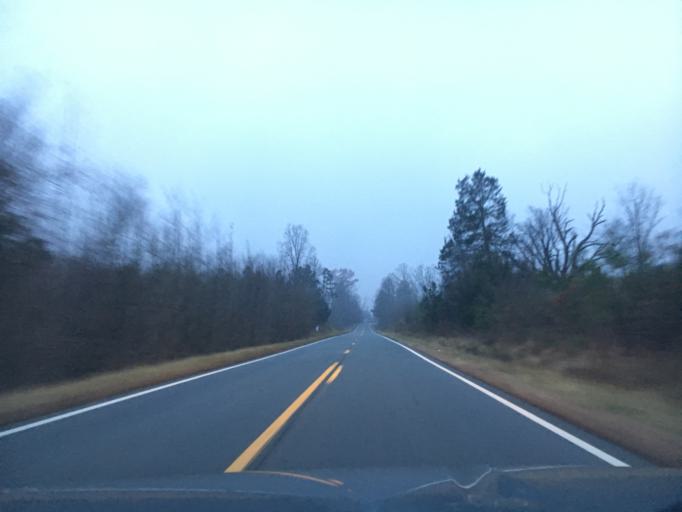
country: US
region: Virginia
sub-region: Halifax County
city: Mountain Road
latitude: 36.6858
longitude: -78.9905
